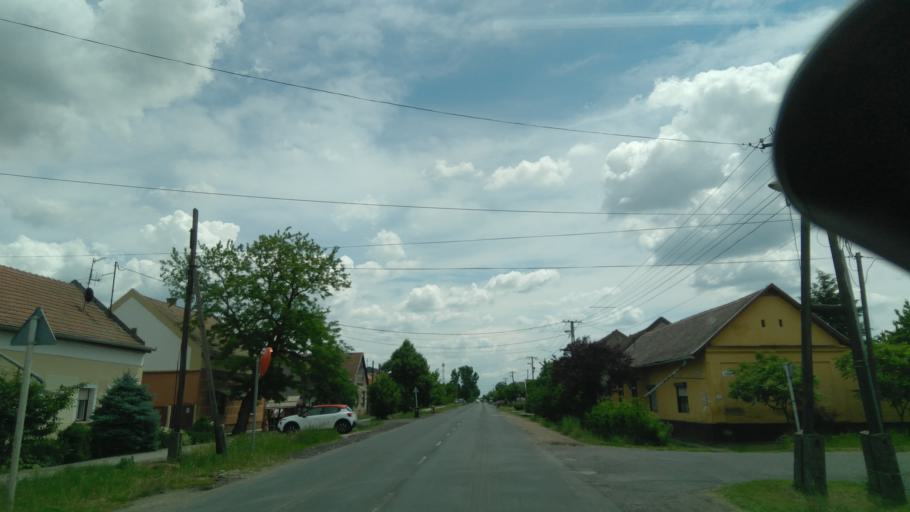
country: HU
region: Bekes
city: Oroshaza
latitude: 46.5470
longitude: 20.6748
